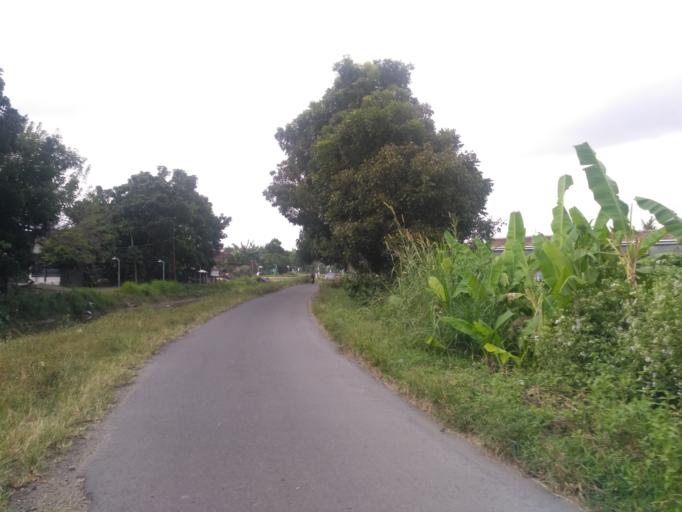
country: ID
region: Daerah Istimewa Yogyakarta
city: Melati
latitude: -7.7527
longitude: 110.3544
